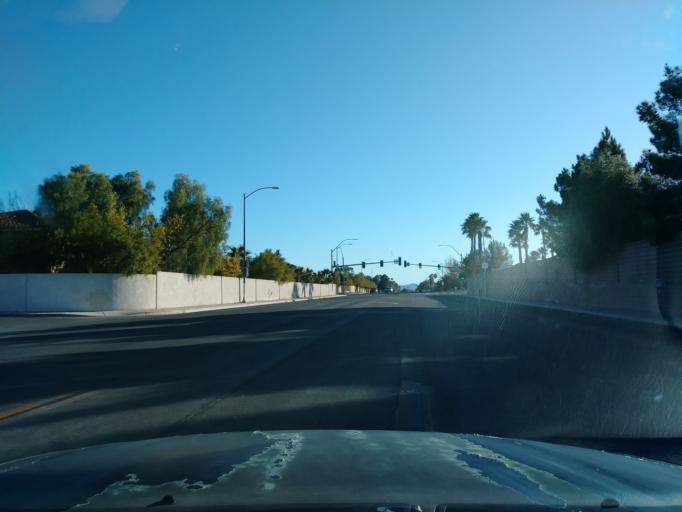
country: US
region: Nevada
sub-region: Clark County
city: Spring Valley
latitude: 36.1525
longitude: -115.2707
